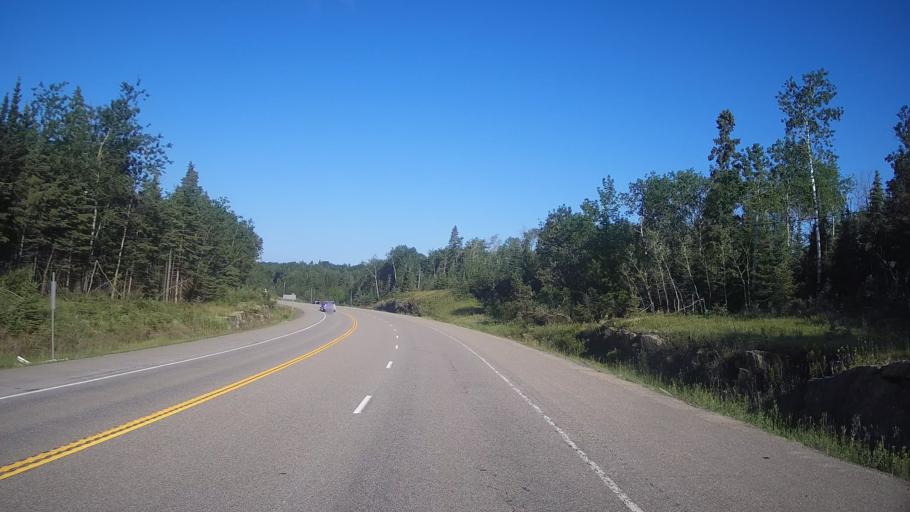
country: US
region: Minnesota
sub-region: Roseau County
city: Warroad
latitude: 49.7189
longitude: -94.7279
